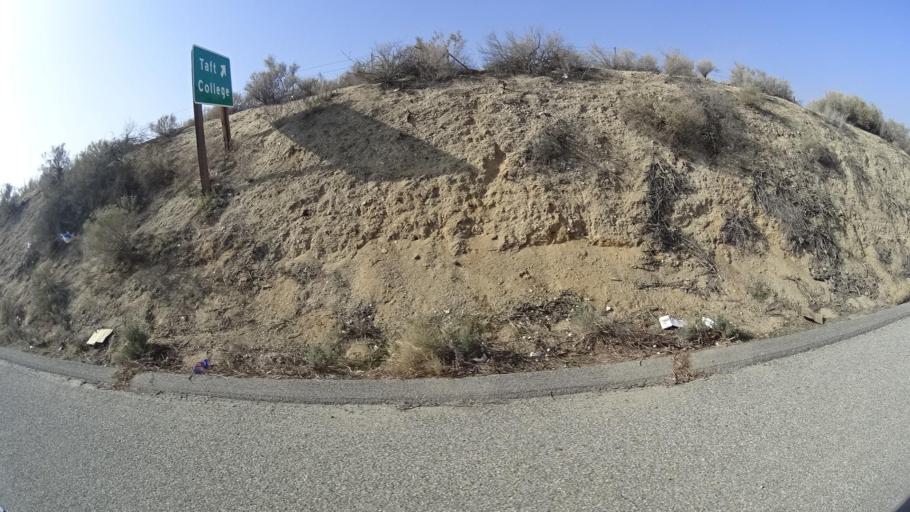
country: US
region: California
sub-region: Kern County
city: Ford City
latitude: 35.1684
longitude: -119.4536
